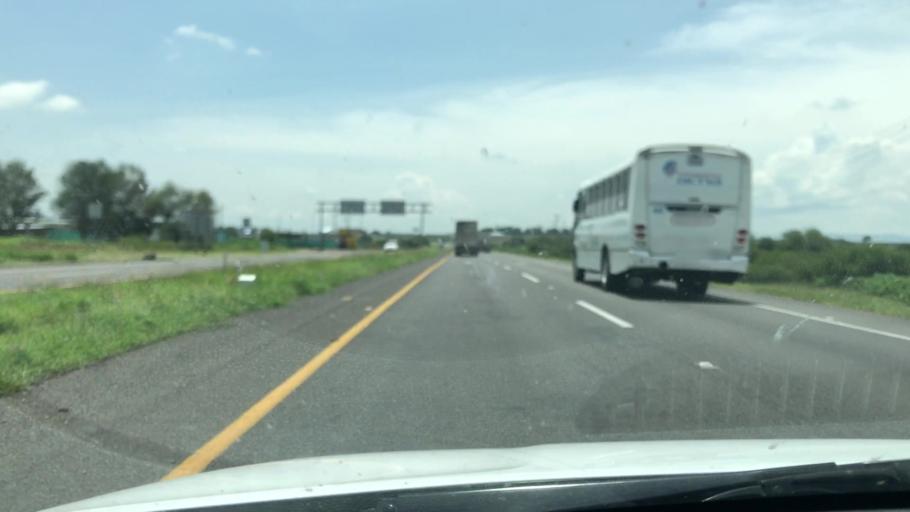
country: MX
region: Guanajuato
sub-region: Penjamo
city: Mezquite de Luna
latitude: 20.3798
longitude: -101.8604
